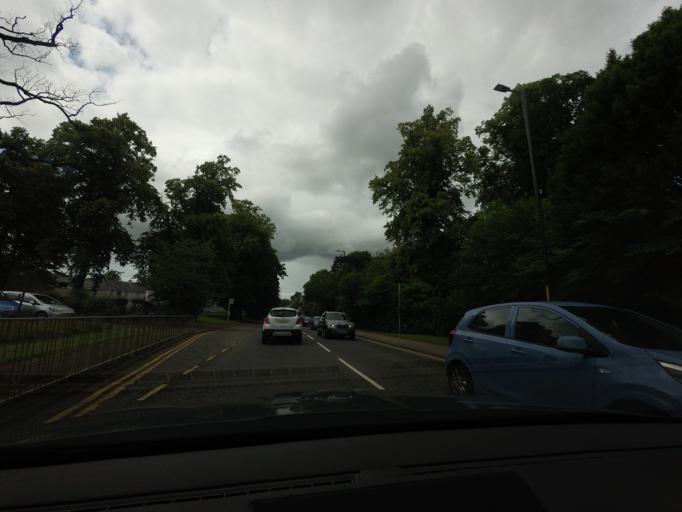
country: GB
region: Scotland
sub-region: Moray
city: Elgin
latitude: 57.6494
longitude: -3.3093
